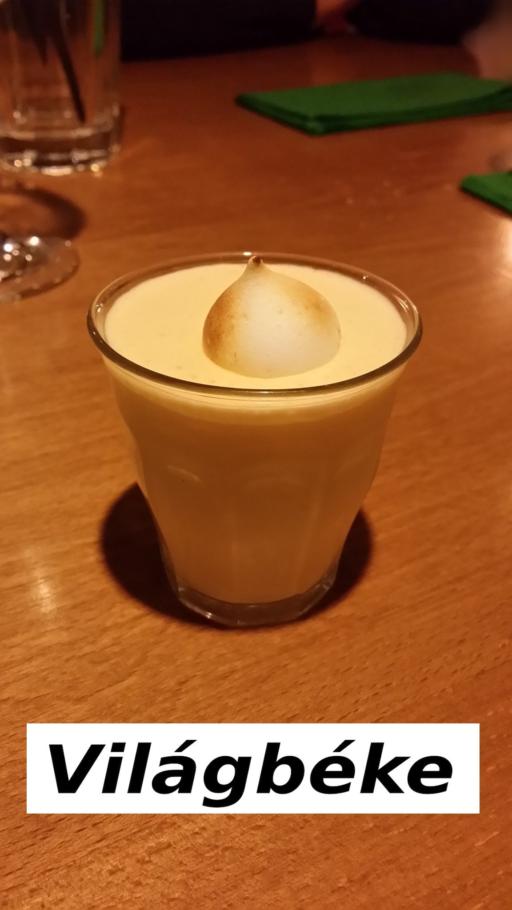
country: HU
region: Borsod-Abauj-Zemplen
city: Encs
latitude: 48.3332
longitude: 21.1165
